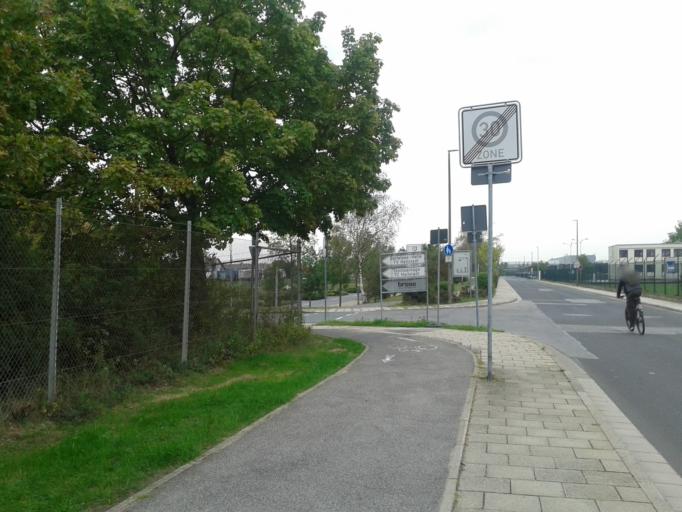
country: DE
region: Bavaria
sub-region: Upper Franconia
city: Hallstadt
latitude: 49.9269
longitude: 10.8911
